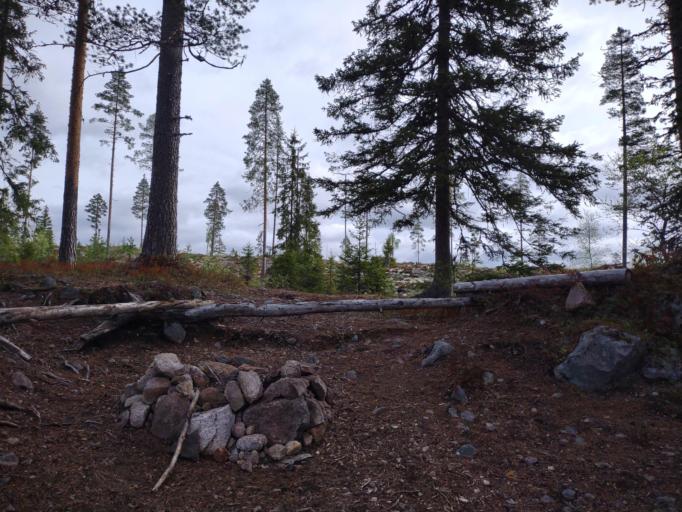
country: NO
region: Oppland
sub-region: Lunner
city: Grua
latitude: 60.2876
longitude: 10.7758
